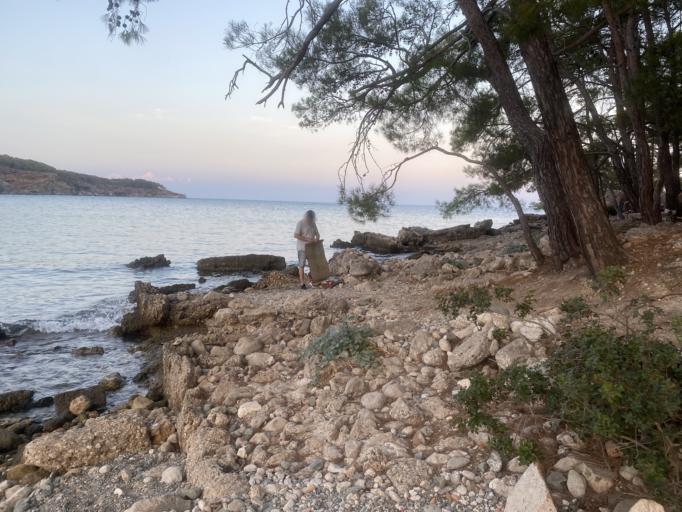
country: TR
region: Antalya
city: Tekirova
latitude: 36.5260
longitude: 30.5519
